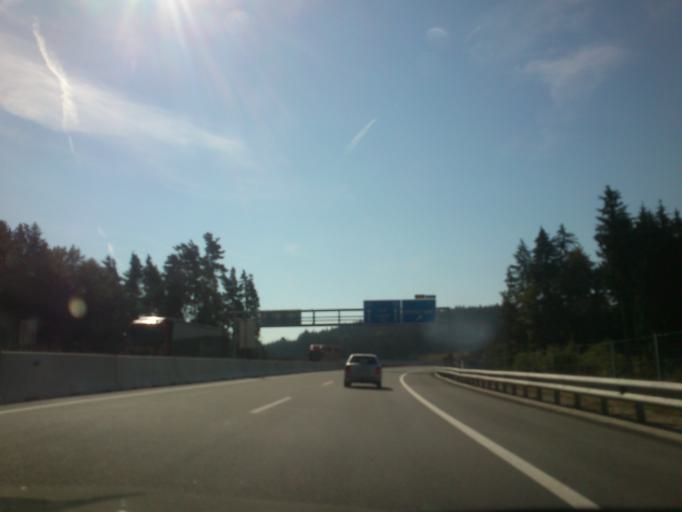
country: AT
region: Upper Austria
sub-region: Politischer Bezirk Freistadt
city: Freistadt
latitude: 48.5214
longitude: 14.5120
